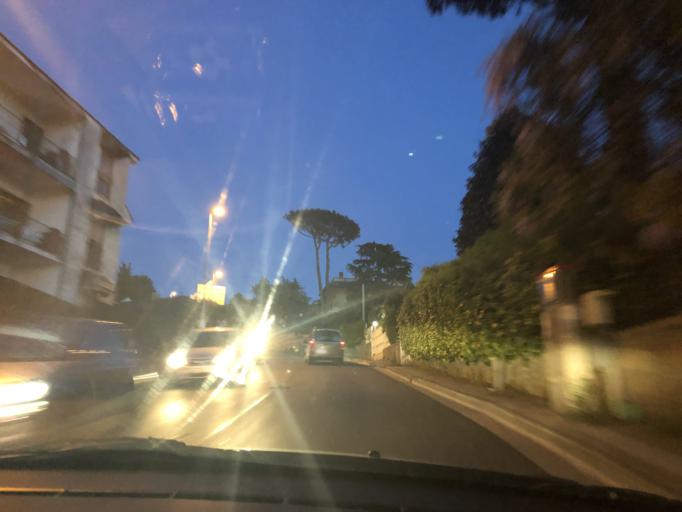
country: IT
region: Campania
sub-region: Provincia di Napoli
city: Marano di Napoli
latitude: 40.8877
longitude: 14.1800
